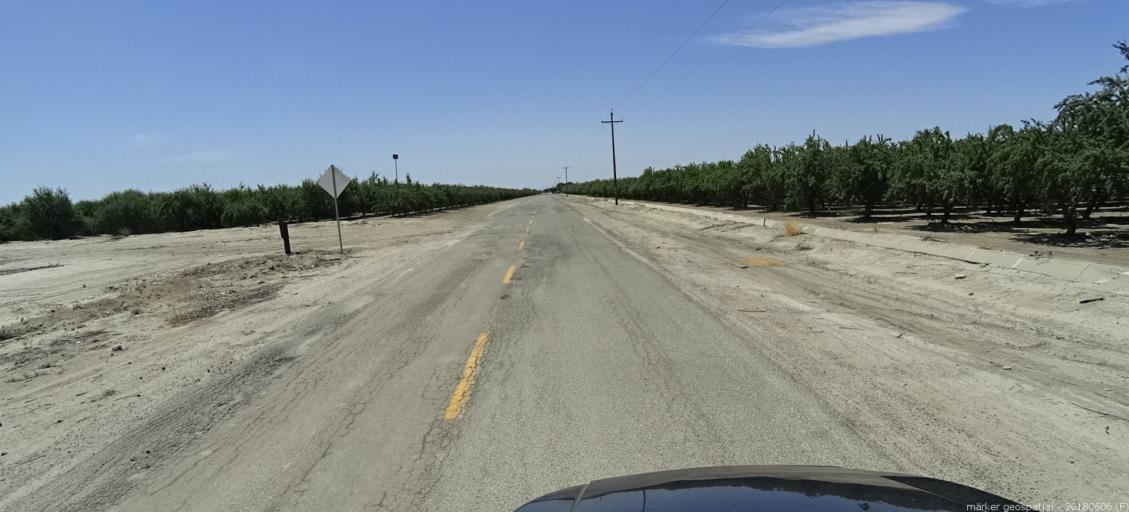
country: US
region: California
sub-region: Fresno County
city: Firebaugh
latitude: 36.8567
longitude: -120.3909
